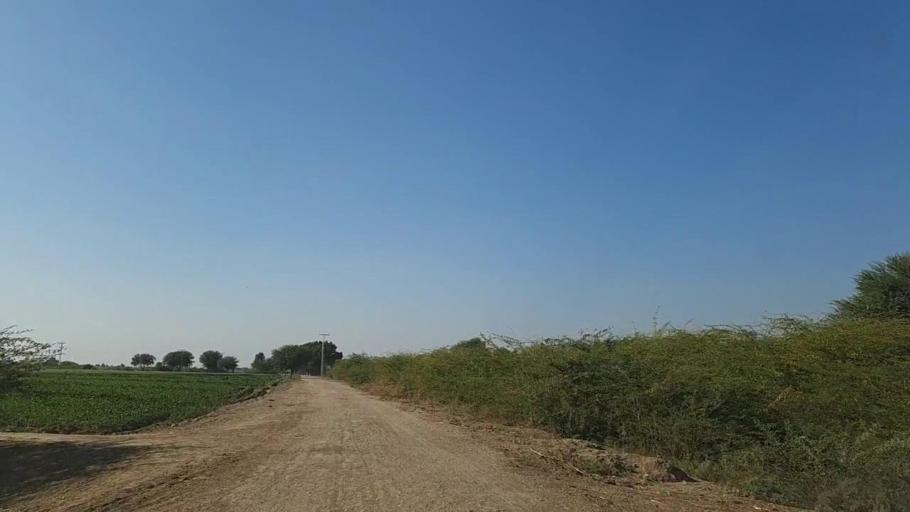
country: PK
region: Sindh
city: Samaro
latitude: 25.3629
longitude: 69.3866
